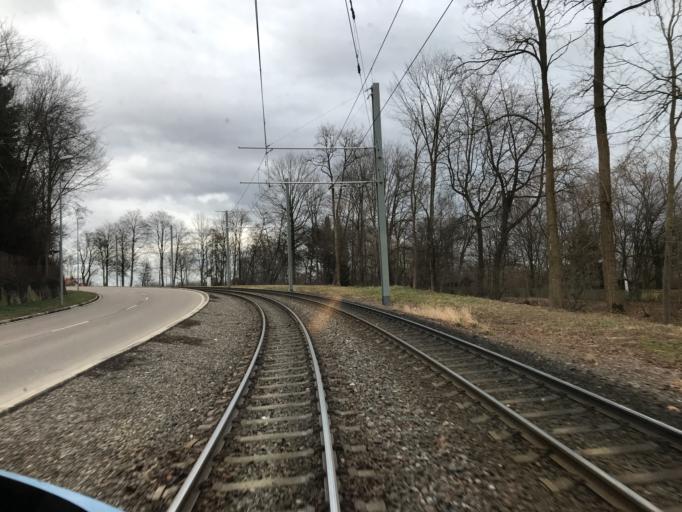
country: DE
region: Bavaria
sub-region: Swabia
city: Neu-Ulm
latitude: 48.4195
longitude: 10.0151
